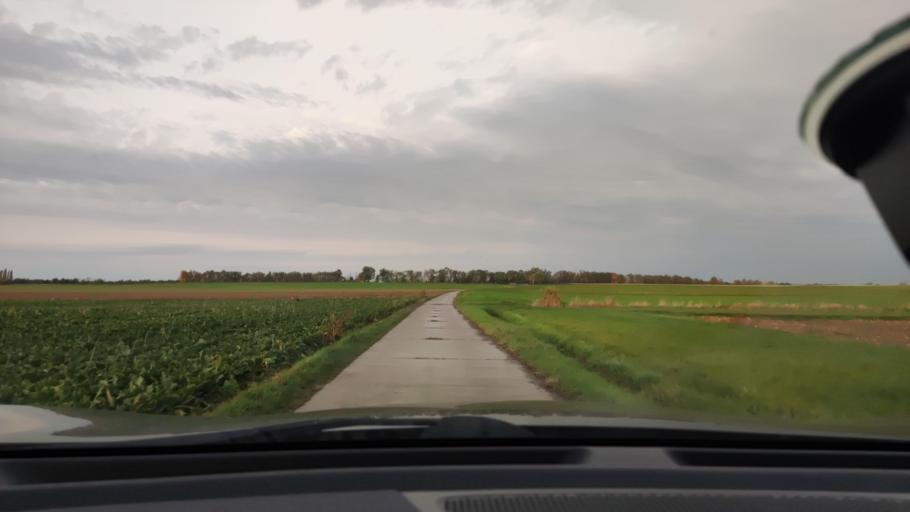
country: BE
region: Flanders
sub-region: Provincie Vlaams-Brabant
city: Tienen
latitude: 50.7726
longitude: 4.9406
